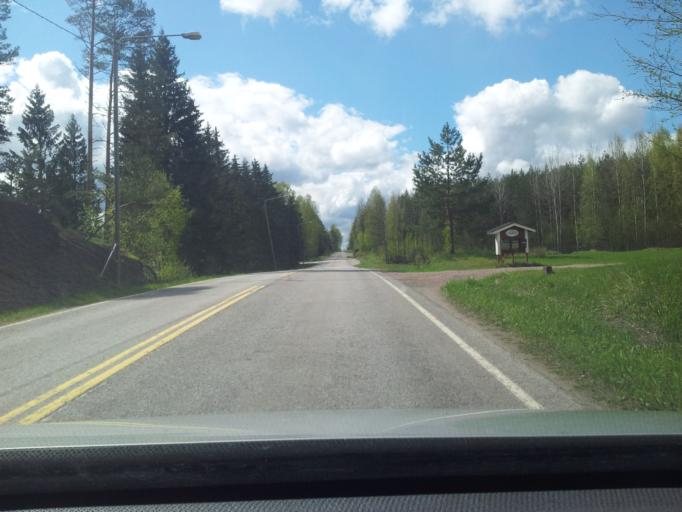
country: FI
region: Uusimaa
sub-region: Loviisa
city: Perna
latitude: 60.5002
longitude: 25.9212
